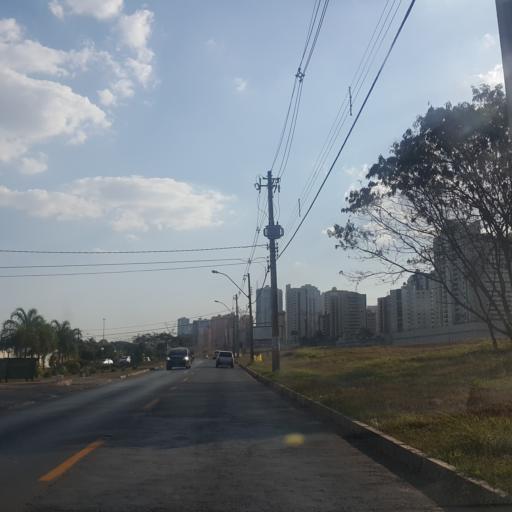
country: BR
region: Federal District
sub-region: Brasilia
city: Brasilia
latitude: -15.8420
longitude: -48.0136
